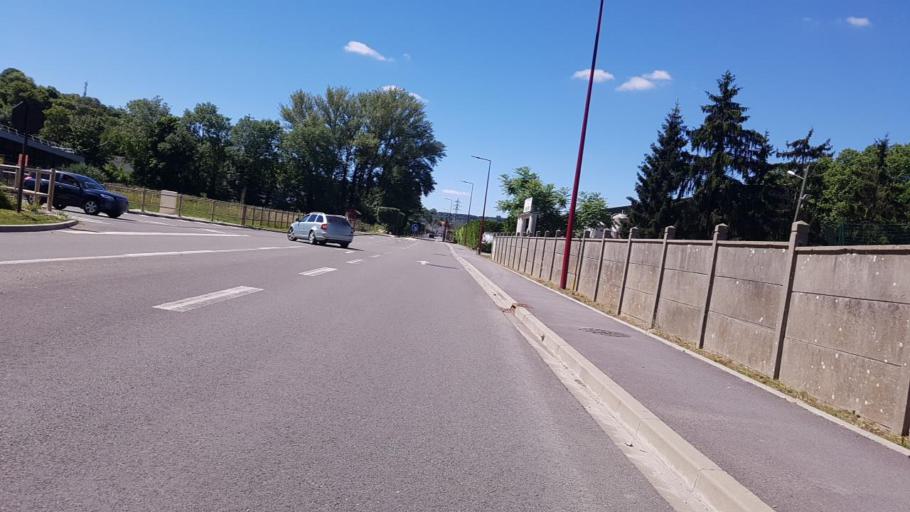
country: FR
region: Ile-de-France
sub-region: Departement de Seine-et-Marne
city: La Ferte-sous-Jouarre
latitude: 48.9561
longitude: 3.1412
